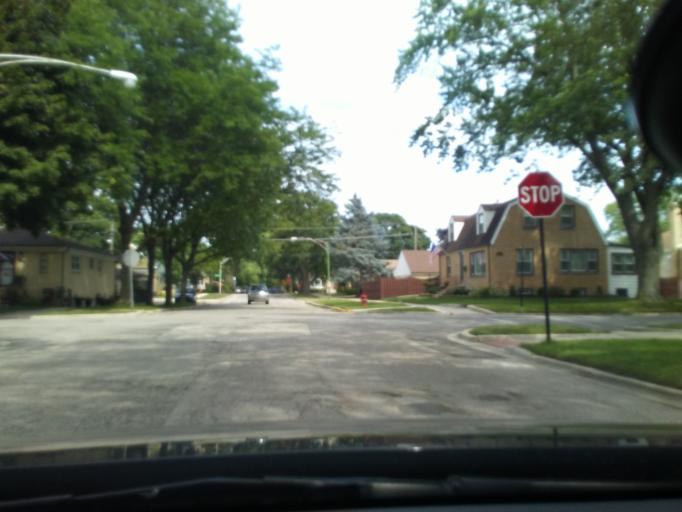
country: US
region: Illinois
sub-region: Cook County
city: Harwood Heights
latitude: 41.9737
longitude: -87.8014
